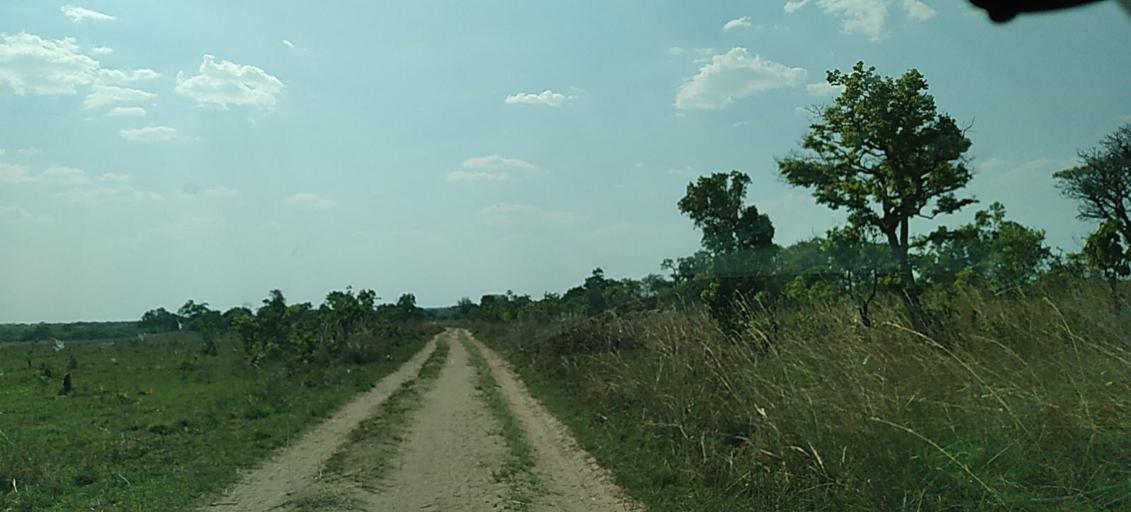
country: ZM
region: North-Western
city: Kalengwa
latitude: -13.1190
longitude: 25.0002
